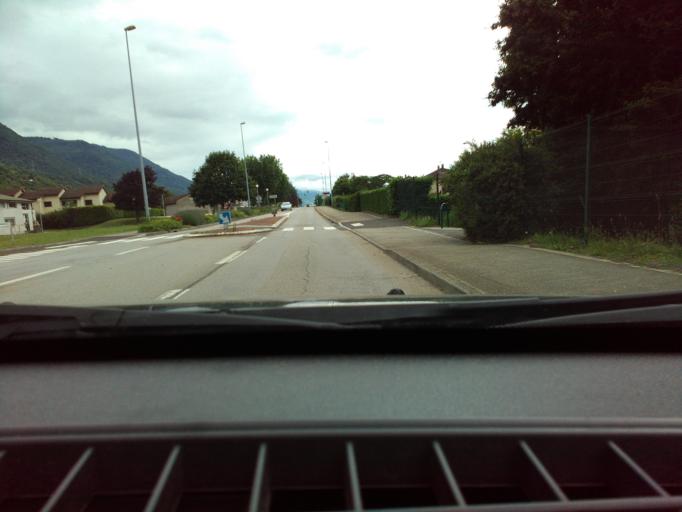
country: FR
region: Rhone-Alpes
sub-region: Departement de l'Isere
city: Le Cheylas
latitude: 45.3740
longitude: 5.9919
